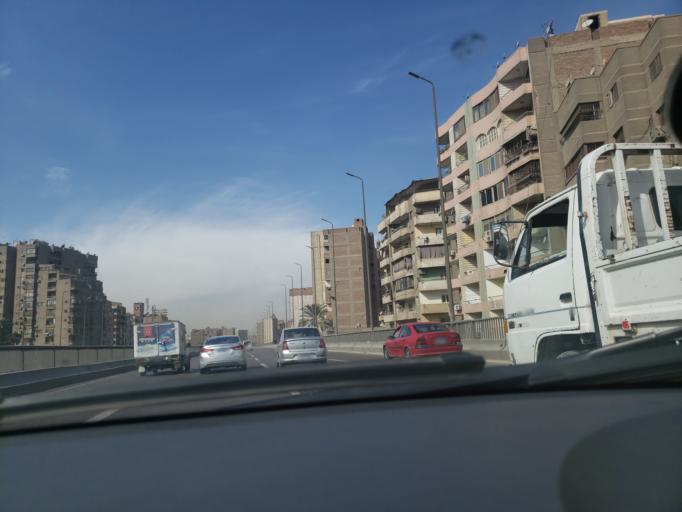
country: EG
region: Al Jizah
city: Al Jizah
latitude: 29.9818
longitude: 31.1570
